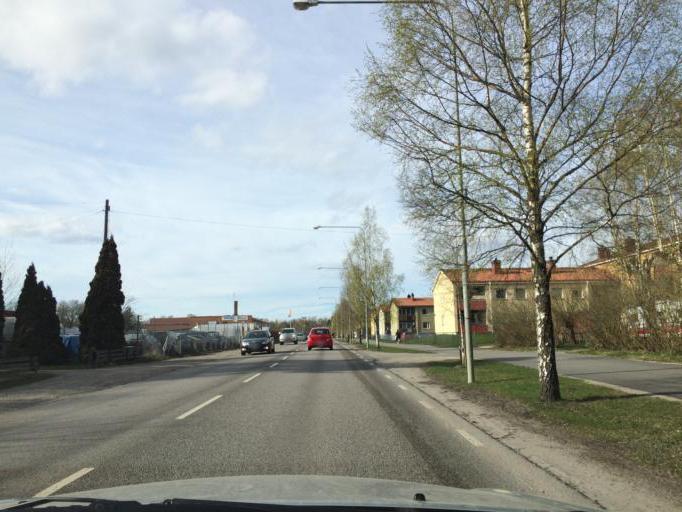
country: SE
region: Soedermanland
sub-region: Eskilstuna Kommun
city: Torshalla
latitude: 59.4132
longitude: 16.4756
